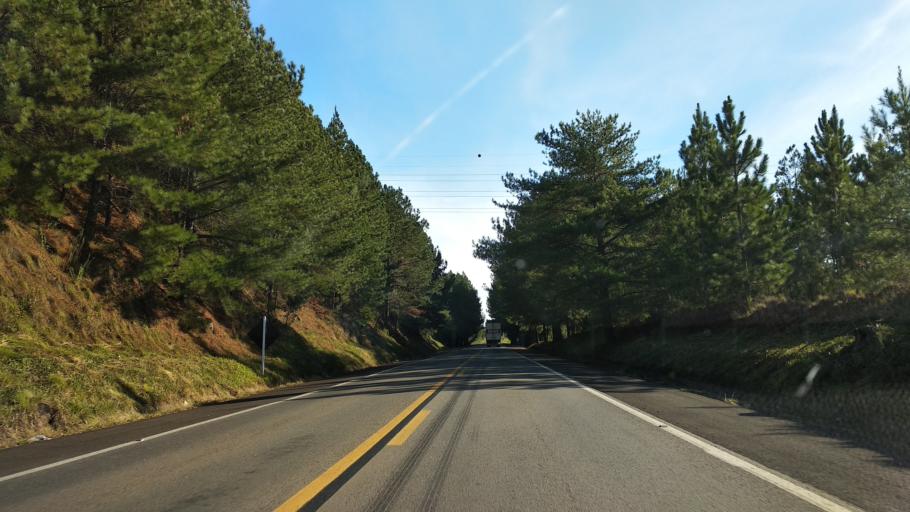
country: BR
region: Santa Catarina
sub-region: Celso Ramos
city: Celso Ramos
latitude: -27.5384
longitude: -51.4079
